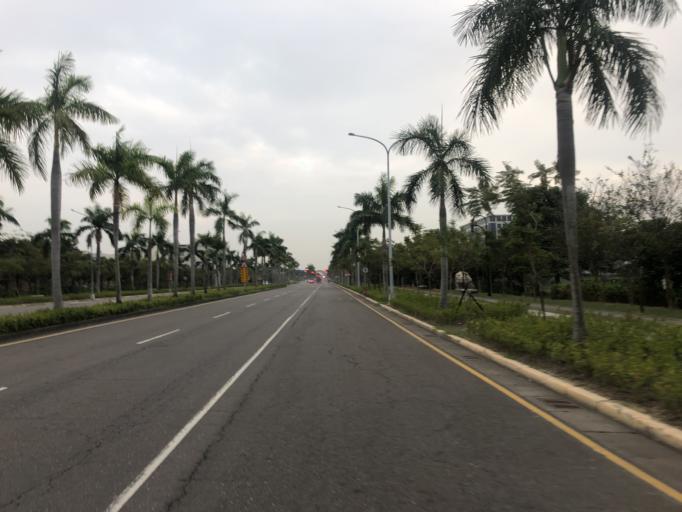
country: TW
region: Taiwan
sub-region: Tainan
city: Tainan
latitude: 23.1014
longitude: 120.2802
